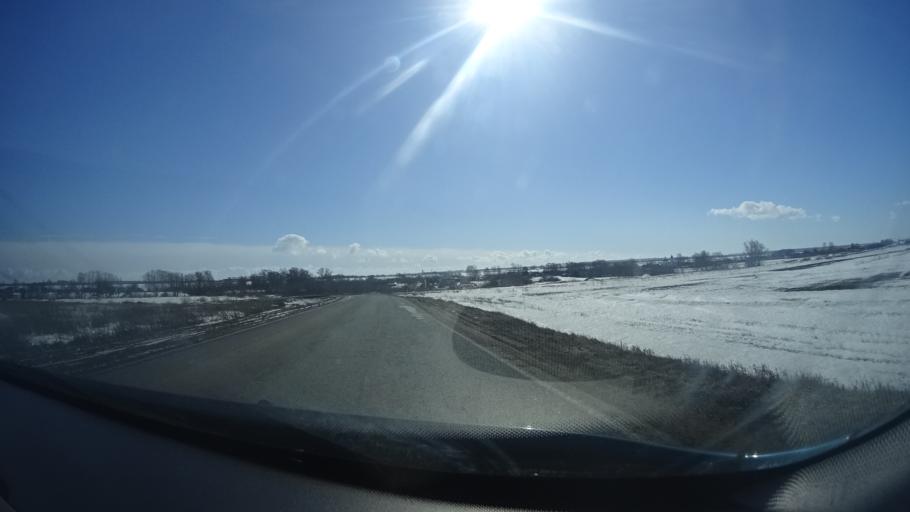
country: RU
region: Bashkortostan
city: Avdon
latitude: 54.5865
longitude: 55.8571
